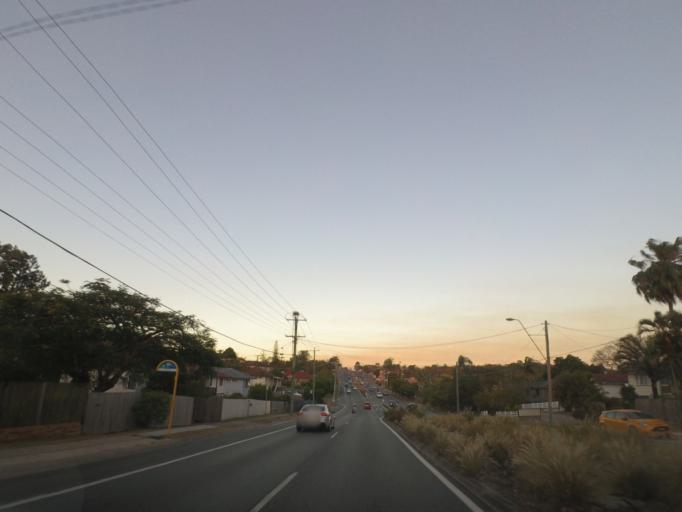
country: AU
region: Queensland
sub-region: Brisbane
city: Upper Mount Gravatt
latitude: -27.5574
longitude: 153.0873
